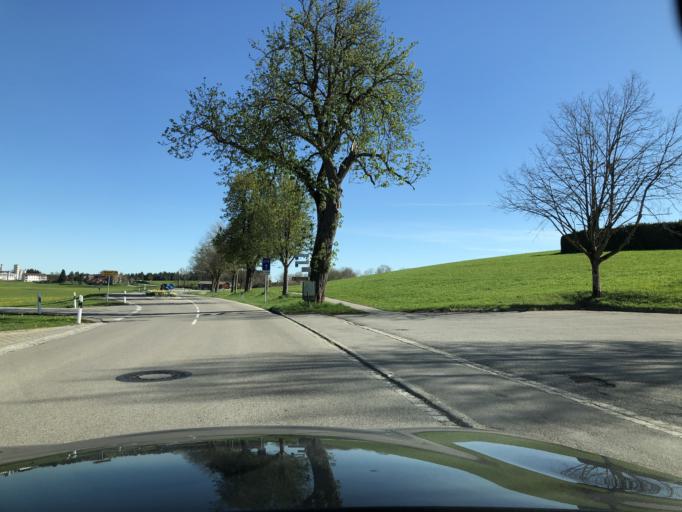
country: DE
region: Bavaria
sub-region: Swabia
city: Ruckholz
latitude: 47.6586
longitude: 10.5400
